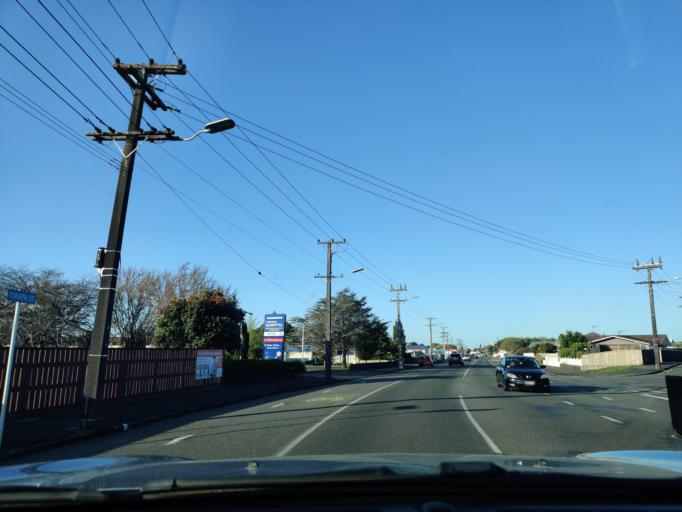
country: NZ
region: Taranaki
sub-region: New Plymouth District
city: New Plymouth
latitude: -39.0751
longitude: 174.0572
